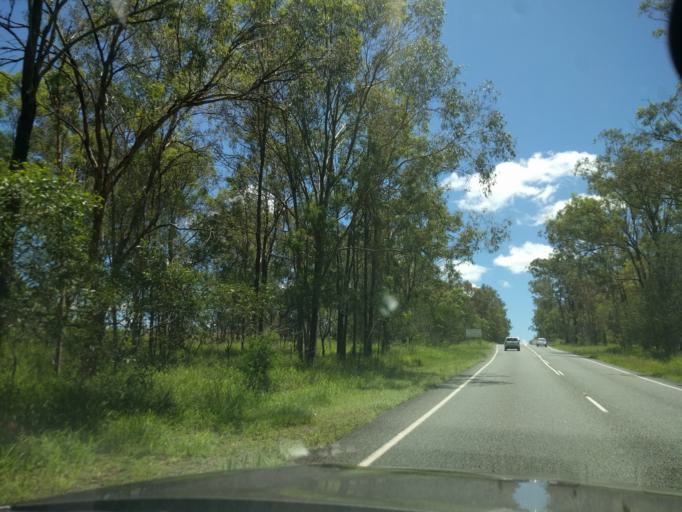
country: AU
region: Queensland
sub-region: Logan
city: Cedar Vale
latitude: -27.8555
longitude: 153.0089
